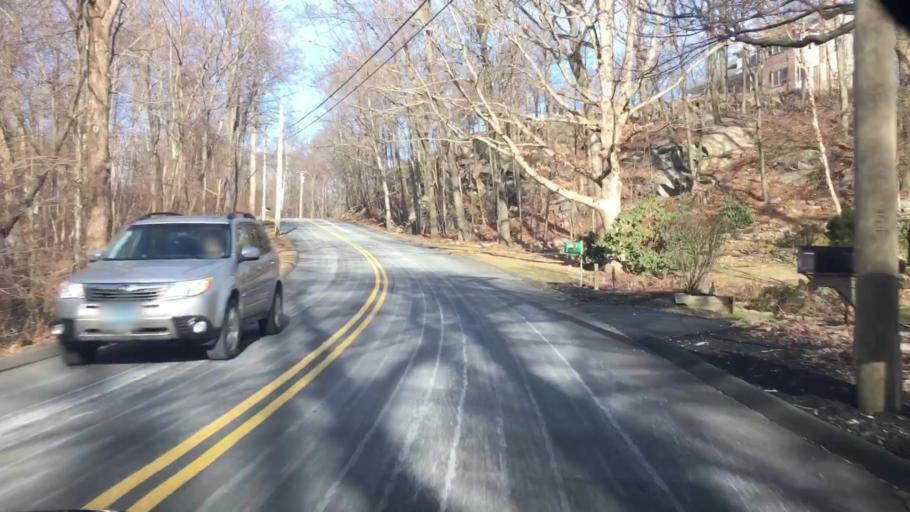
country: US
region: Connecticut
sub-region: New Haven County
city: Prospect
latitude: 41.5314
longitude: -72.9564
